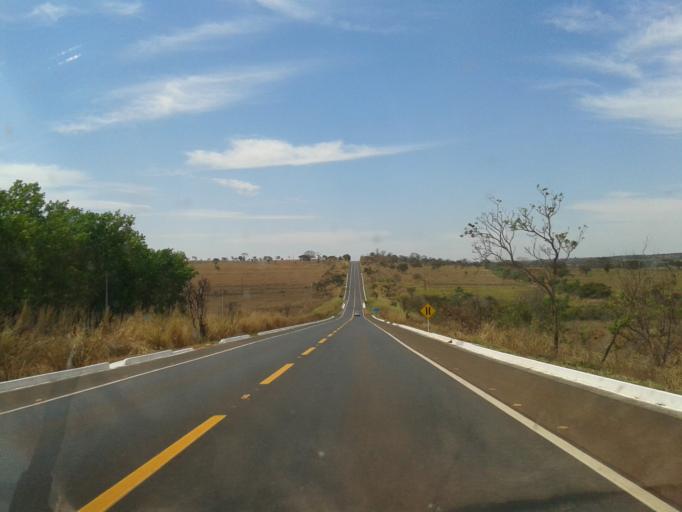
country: BR
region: Minas Gerais
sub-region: Monte Alegre De Minas
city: Monte Alegre de Minas
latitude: -18.8793
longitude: -49.0976
